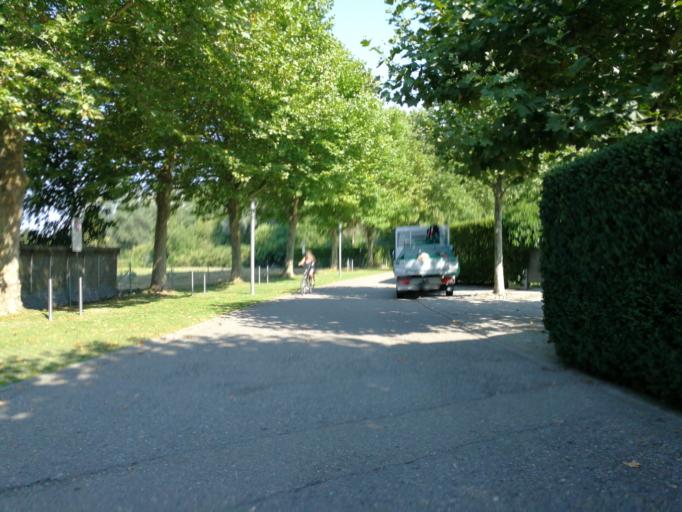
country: CH
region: Saint Gallen
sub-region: Wahlkreis See-Gaster
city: Rapperswil
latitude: 47.2147
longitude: 8.8056
